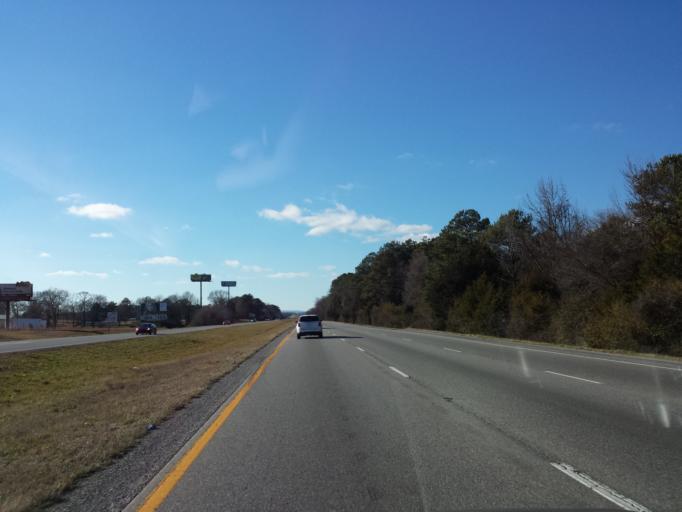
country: US
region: Alabama
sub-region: Saint Clair County
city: Riverside
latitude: 33.5920
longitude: -86.1652
